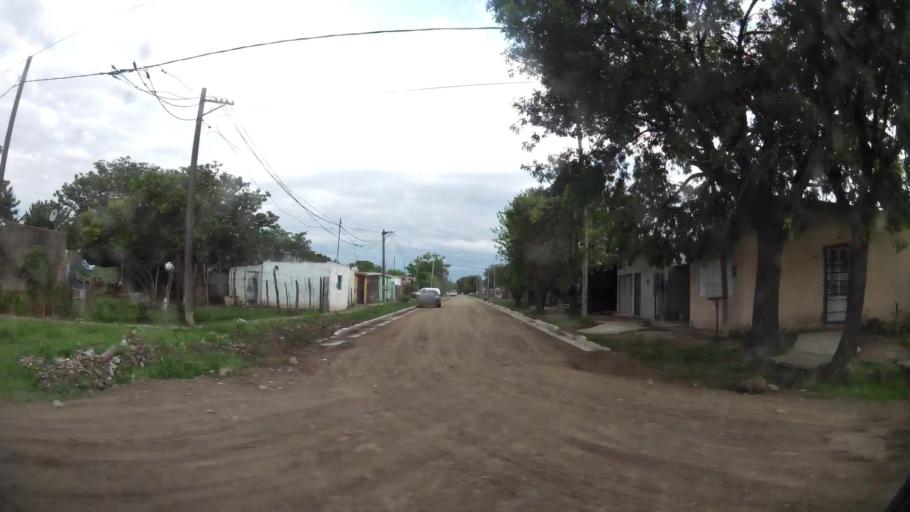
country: AR
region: Buenos Aires
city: San Nicolas de los Arroyos
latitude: -33.3162
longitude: -60.2443
